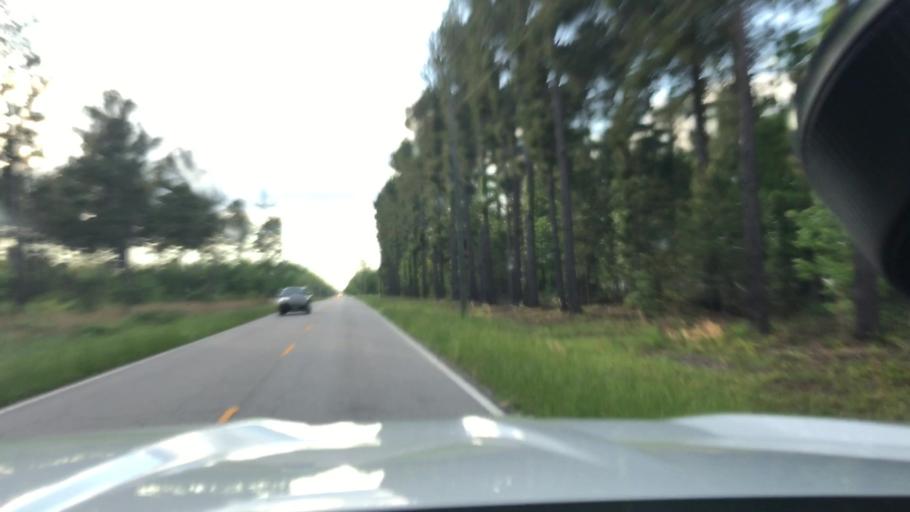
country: US
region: South Carolina
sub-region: Bamberg County
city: Denmark
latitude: 33.4609
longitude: -81.1512
